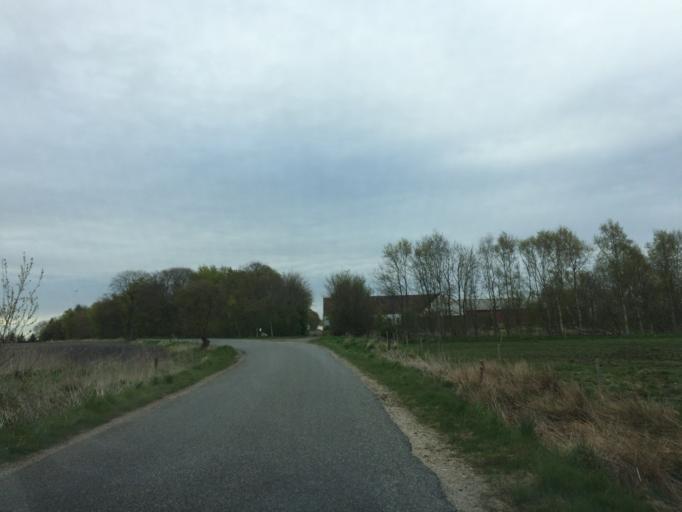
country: DK
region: Central Jutland
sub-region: Viborg Kommune
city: Karup
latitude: 56.3491
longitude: 9.0861
